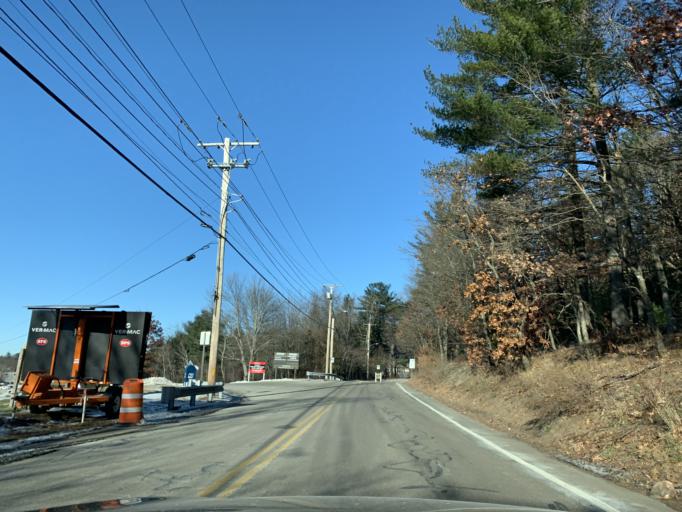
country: US
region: Massachusetts
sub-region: Norfolk County
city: Norwood
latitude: 42.2015
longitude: -71.1624
